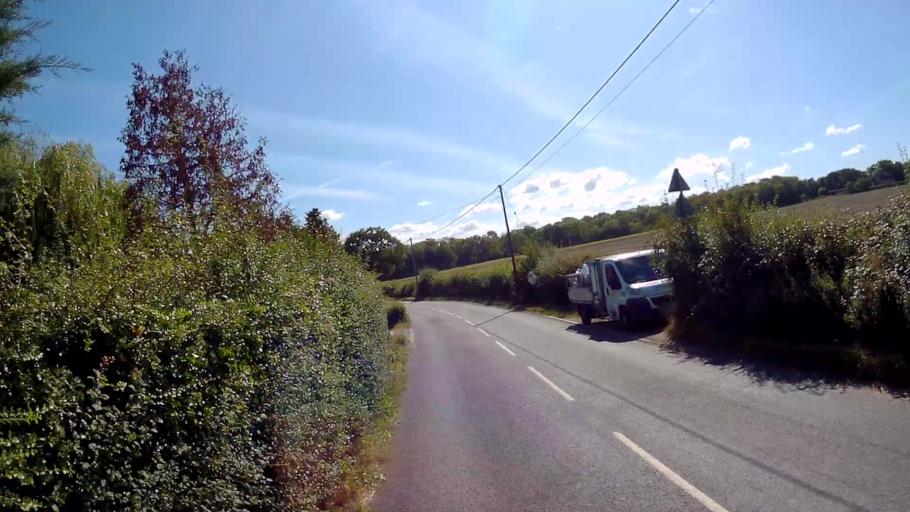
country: GB
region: England
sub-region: West Berkshire
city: Stratfield Mortimer
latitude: 51.3722
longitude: -1.0341
